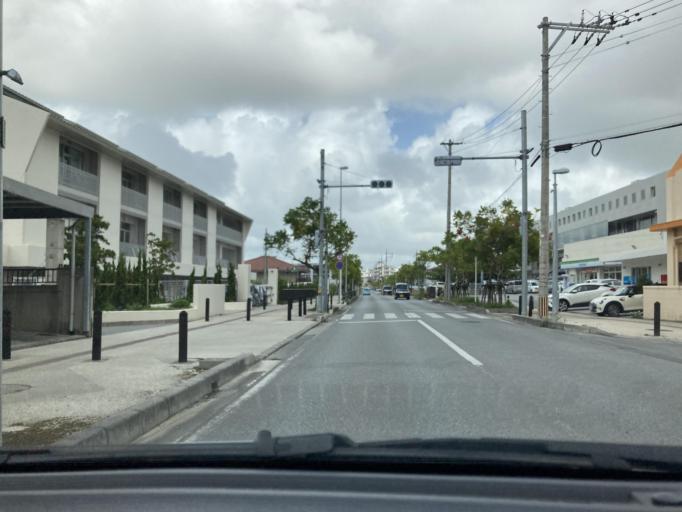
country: JP
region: Okinawa
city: Ginowan
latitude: 26.2299
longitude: 127.7326
